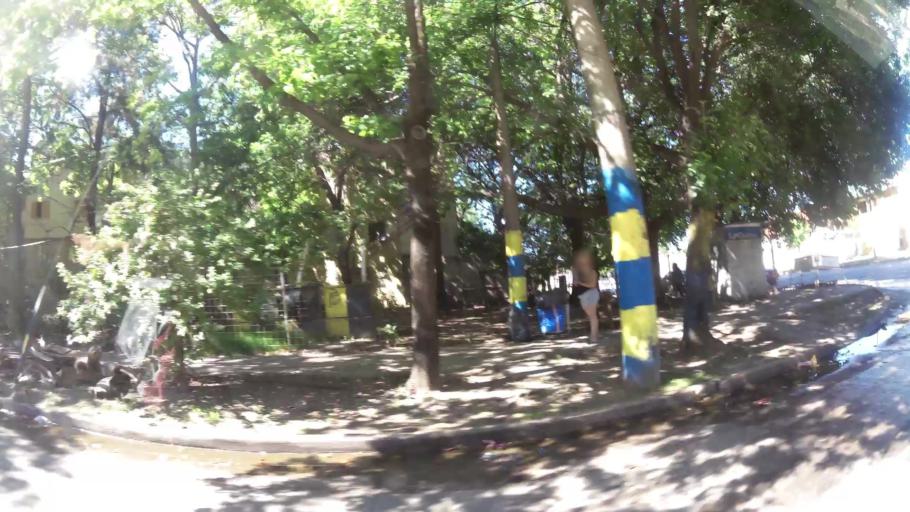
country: AR
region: Santa Fe
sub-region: Departamento de Rosario
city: Rosario
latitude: -32.9732
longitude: -60.7008
